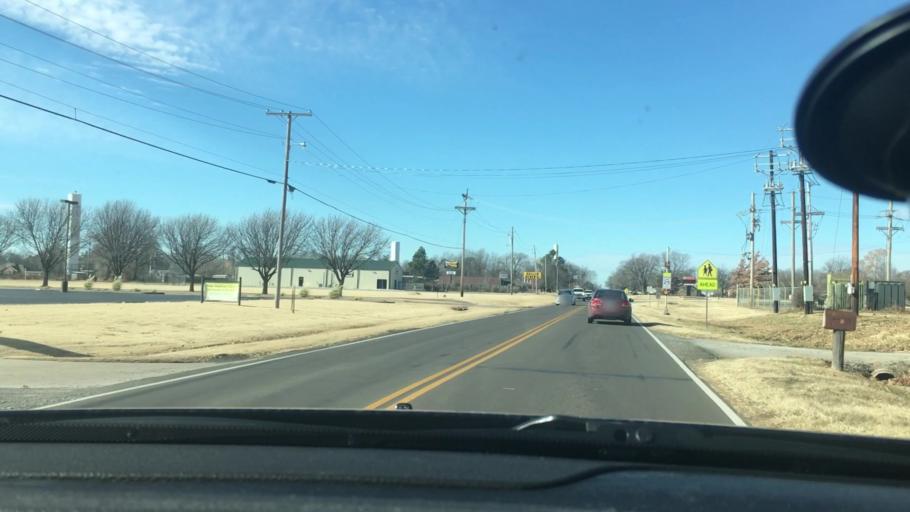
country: US
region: Oklahoma
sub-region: Cleveland County
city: Lexington
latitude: 35.0150
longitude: -97.3227
